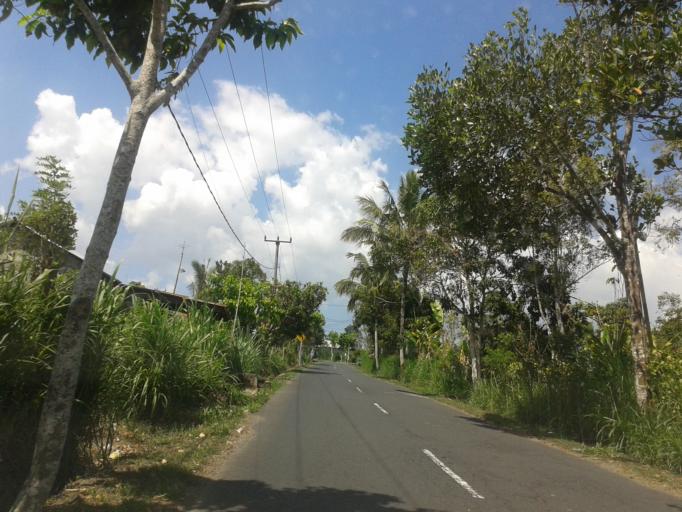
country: ID
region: Bali
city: Banjar Tiga
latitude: -8.3302
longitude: 115.3247
